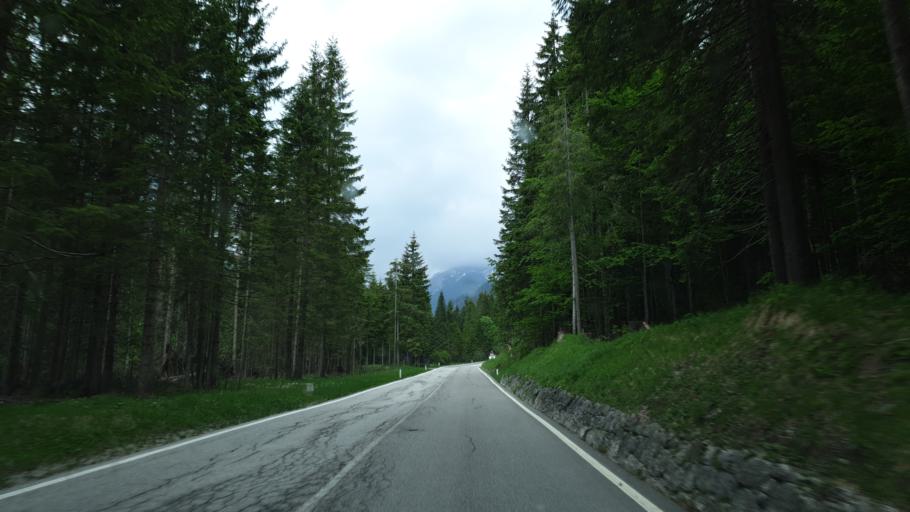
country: IT
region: Veneto
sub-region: Provincia di Belluno
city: San Vito
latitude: 46.5352
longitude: 12.2601
